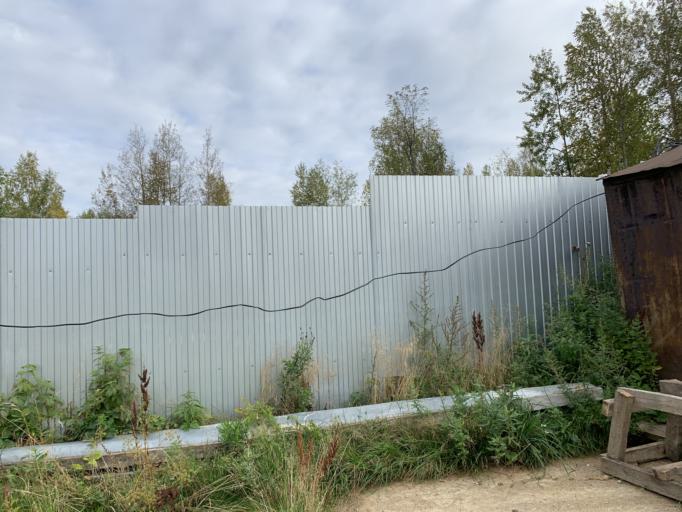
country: RU
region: Perm
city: Gubakha
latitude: 58.8310
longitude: 57.5609
